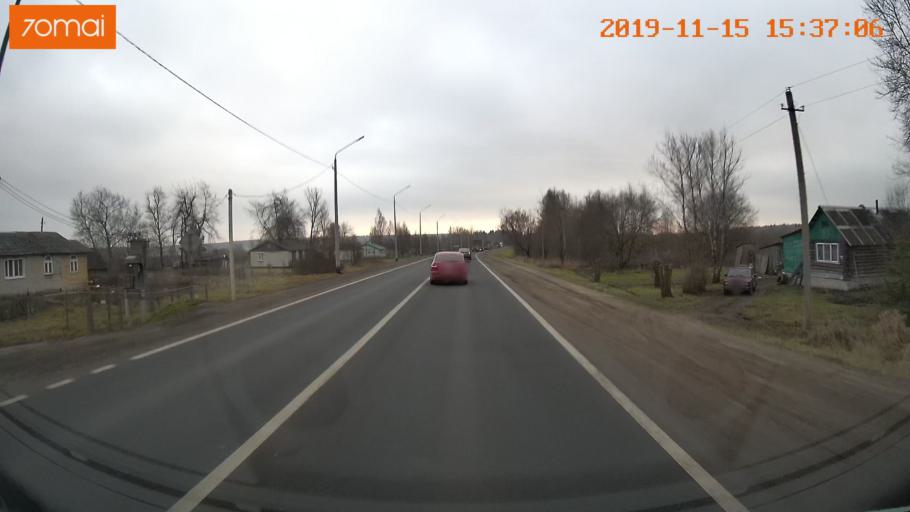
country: RU
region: Jaroslavl
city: Danilov
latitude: 58.0426
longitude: 40.0904
